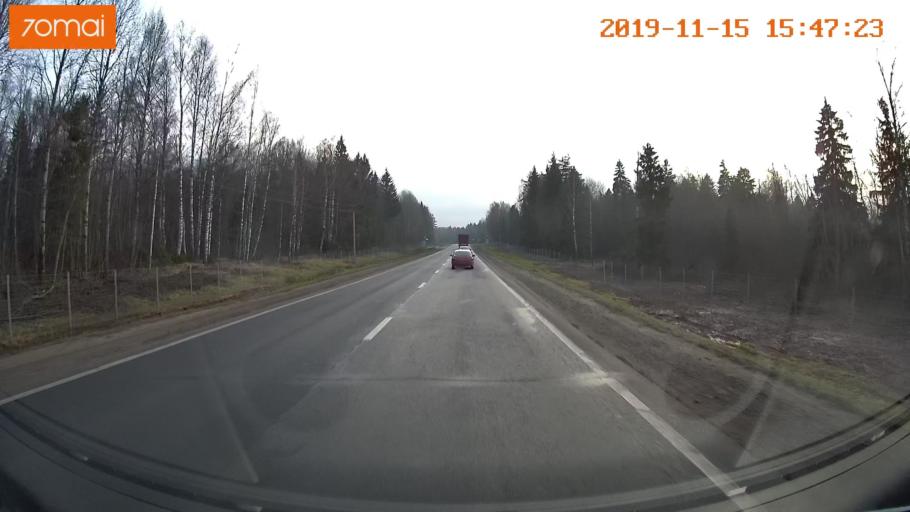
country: RU
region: Jaroslavl
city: Danilov
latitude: 57.9387
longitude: 40.0101
